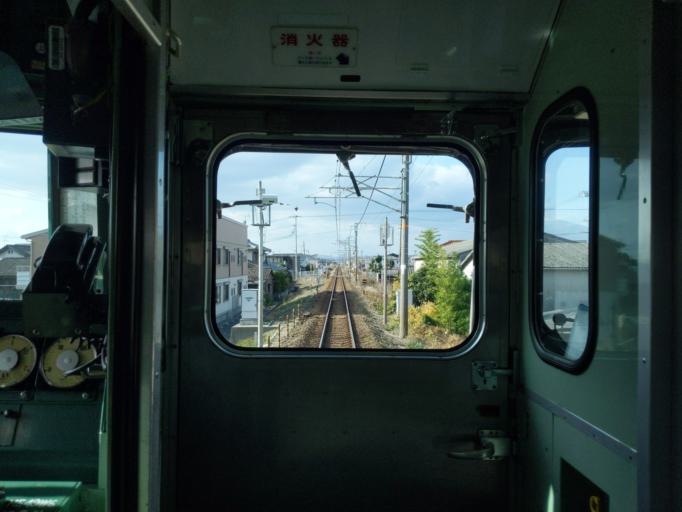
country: JP
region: Okayama
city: Okayama-shi
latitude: 34.6063
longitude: 133.8584
